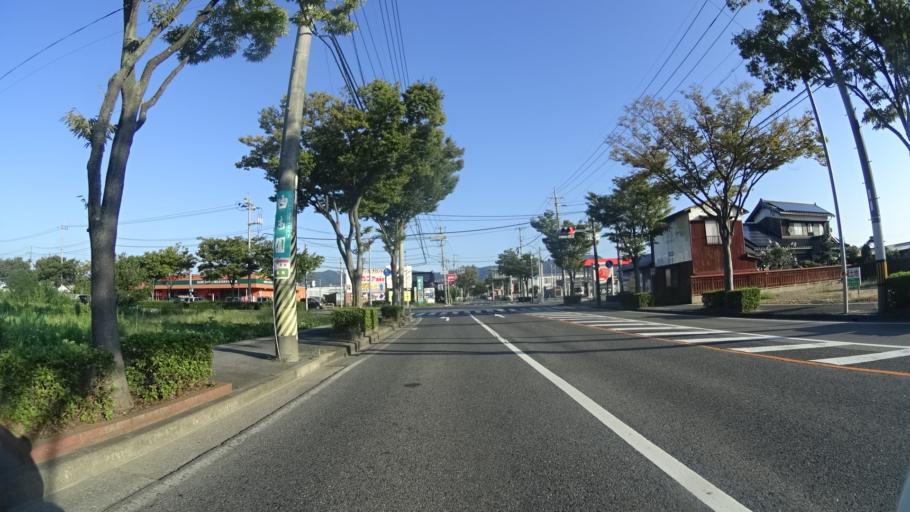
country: JP
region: Shimane
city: Sakaiminato
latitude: 35.5218
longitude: 133.2135
